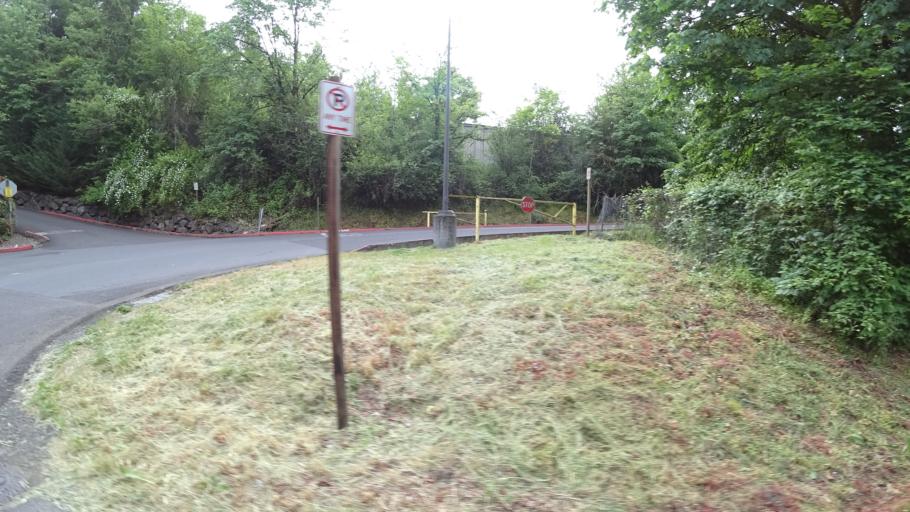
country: US
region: Oregon
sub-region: Clackamas County
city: Lake Oswego
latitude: 45.4283
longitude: -122.7038
